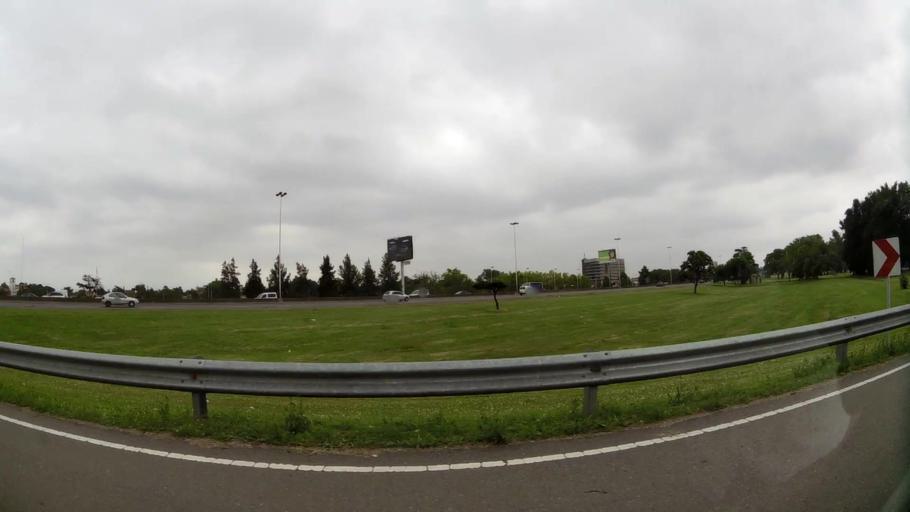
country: AR
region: Buenos Aires
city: San Justo
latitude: -34.7376
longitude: -58.5187
